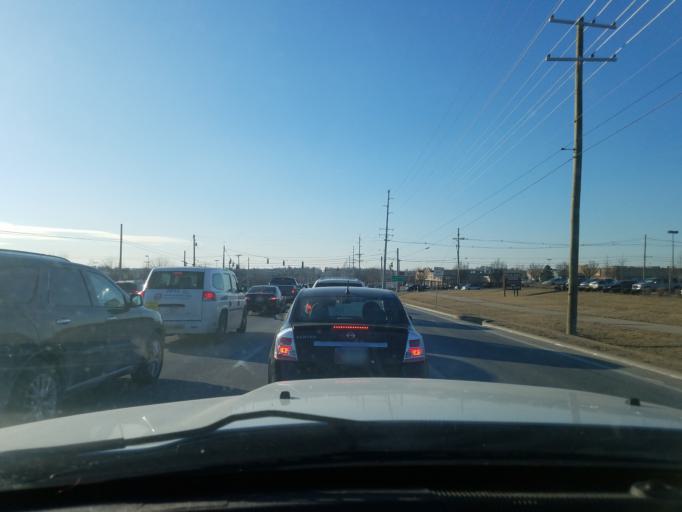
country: US
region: Kentucky
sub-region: Jefferson County
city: Middletown
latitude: 38.2426
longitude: -85.5082
